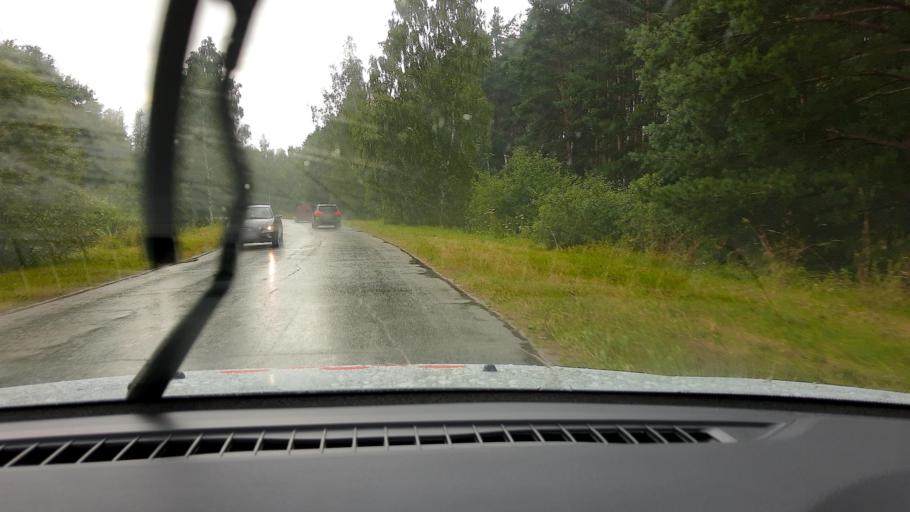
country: RU
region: Nizjnij Novgorod
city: Surovatikha
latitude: 55.9527
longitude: 43.9572
